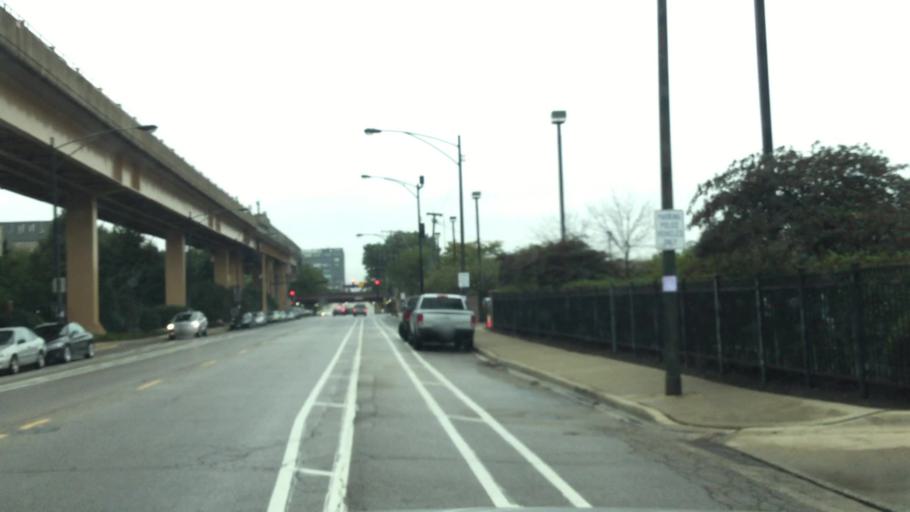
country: US
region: Illinois
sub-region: Cook County
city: Chicago
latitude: 41.8578
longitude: -87.6281
